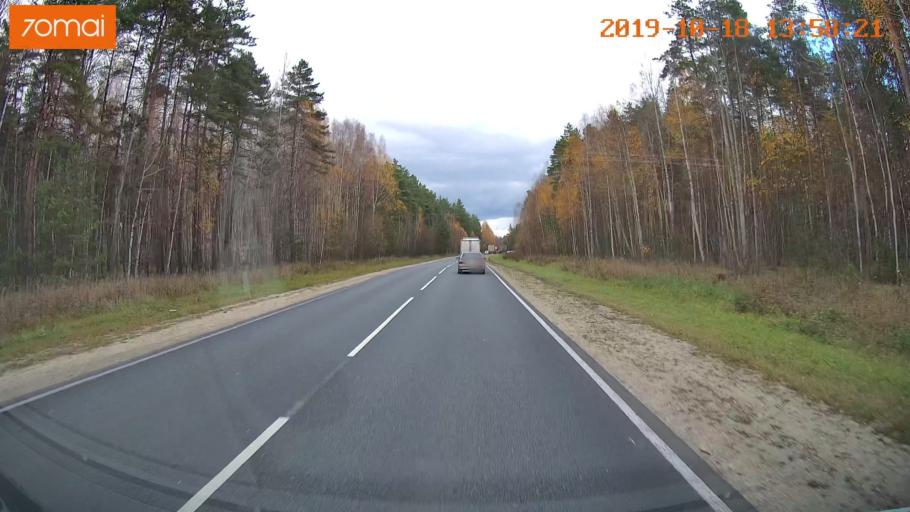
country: RU
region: Rjazan
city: Spas-Klepiki
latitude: 55.0838
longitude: 40.0535
